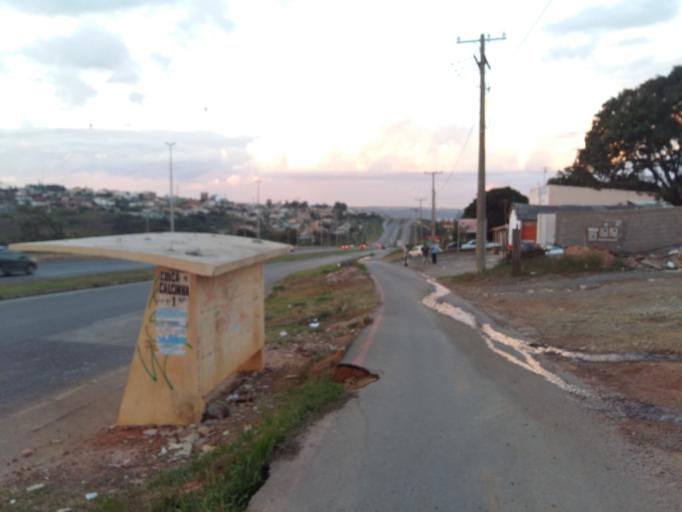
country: BR
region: Federal District
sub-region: Brasilia
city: Brasilia
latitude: -15.6803
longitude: -47.8491
